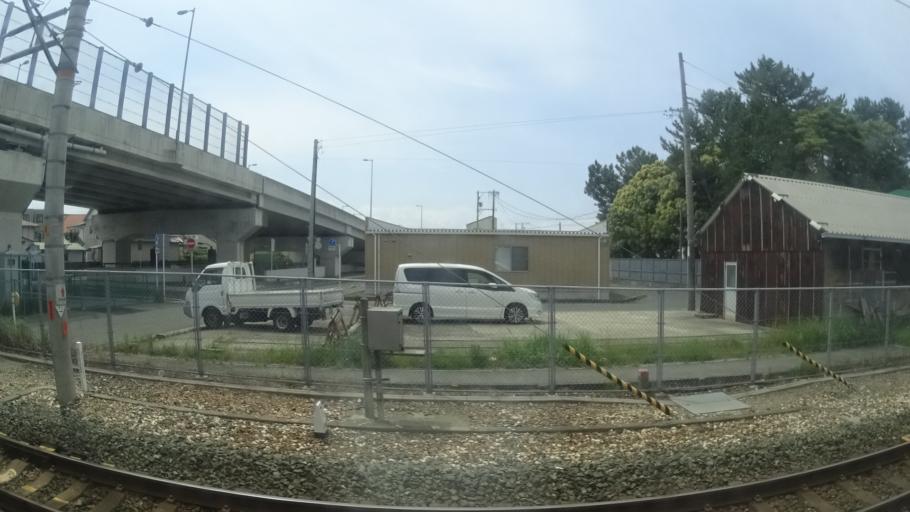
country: JP
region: Shizuoka
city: Hamamatsu
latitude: 34.6905
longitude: 137.6779
